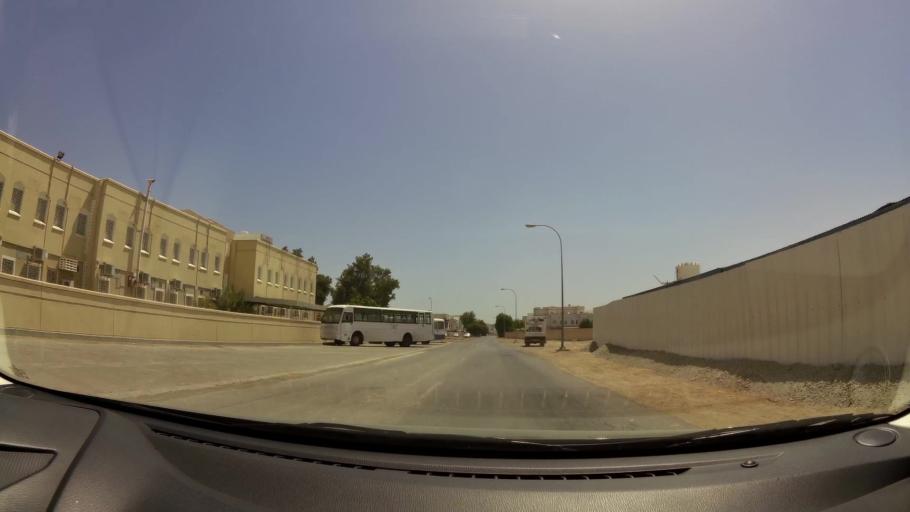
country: OM
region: Muhafazat Masqat
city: As Sib al Jadidah
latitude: 23.6238
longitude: 58.2497
